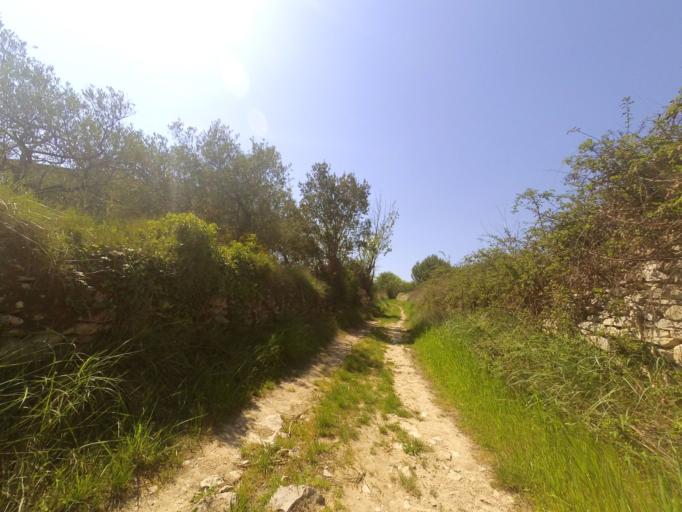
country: FR
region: Languedoc-Roussillon
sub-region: Departement du Gard
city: Congenies
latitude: 43.7789
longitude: 4.1665
